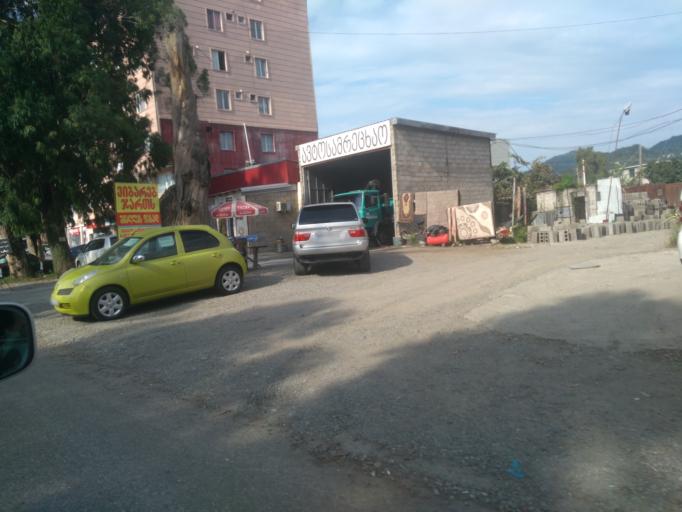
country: GE
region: Ajaria
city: Khelvachauri
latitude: 41.5883
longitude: 41.6489
